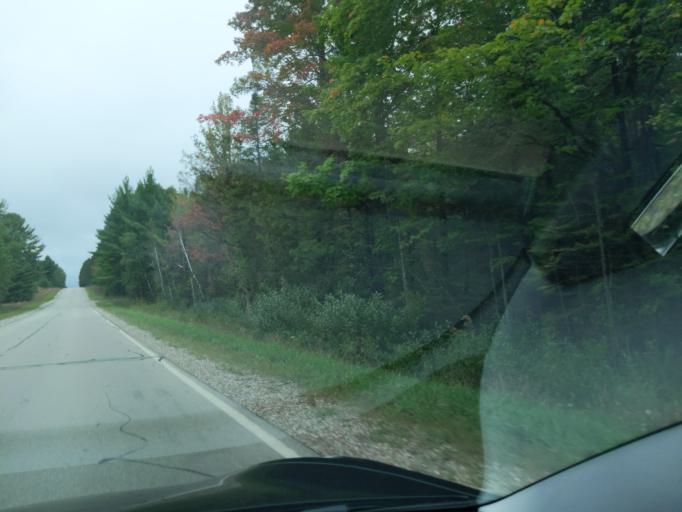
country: US
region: Michigan
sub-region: Grand Traverse County
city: Kingsley
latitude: 44.6187
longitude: -85.3532
